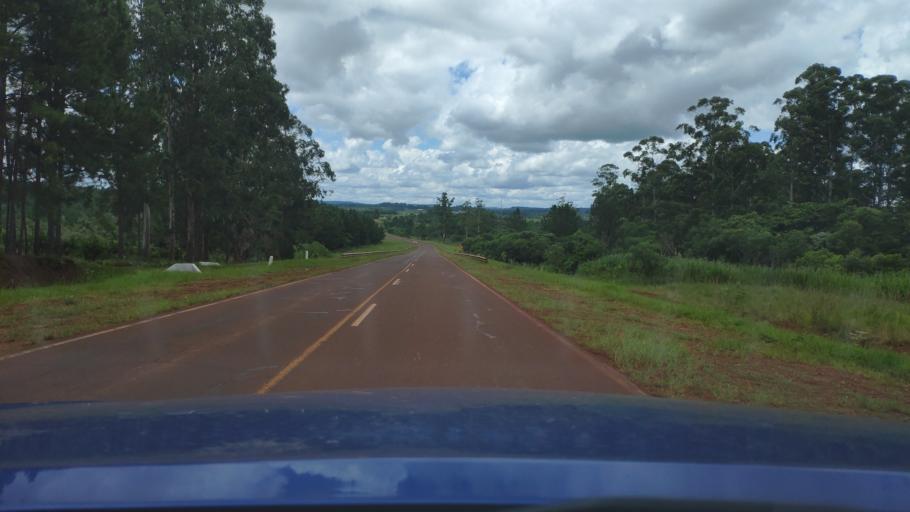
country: AR
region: Misiones
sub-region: Departamento de San Javier
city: San Javier
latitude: -27.8537
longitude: -55.2489
